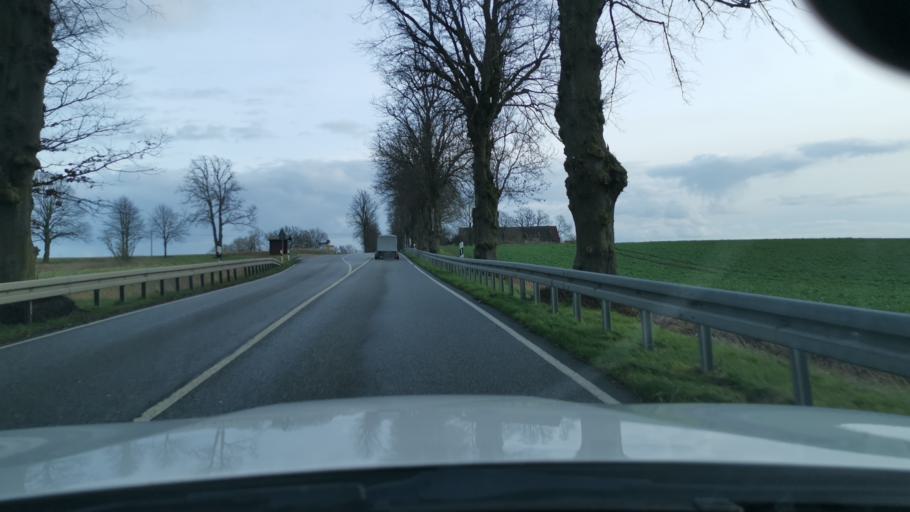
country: DE
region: Mecklenburg-Vorpommern
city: Laage
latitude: 53.9594
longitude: 12.2973
